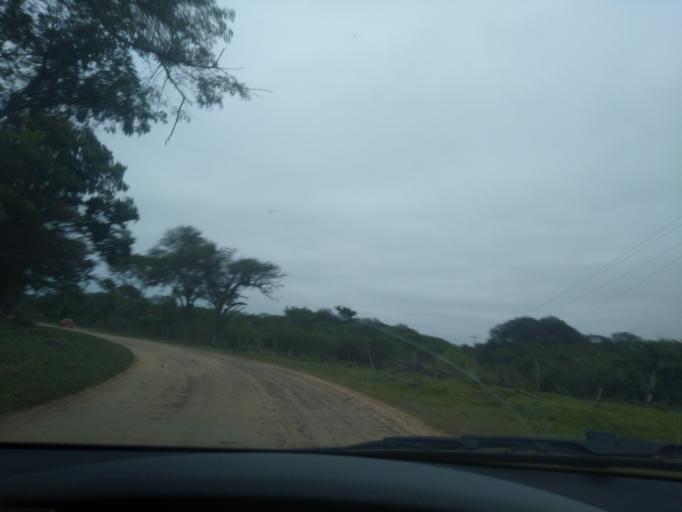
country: AR
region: Chaco
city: Colonia Benitez
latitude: -27.3478
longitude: -58.9706
